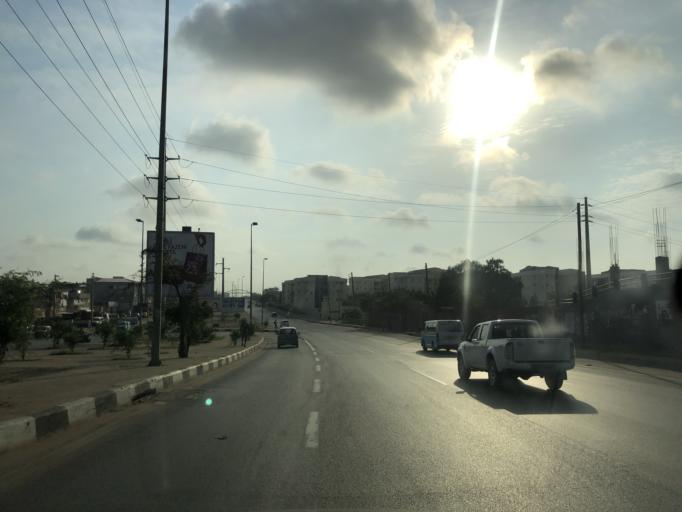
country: AO
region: Luanda
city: Luanda
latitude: -8.8950
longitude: 13.2291
